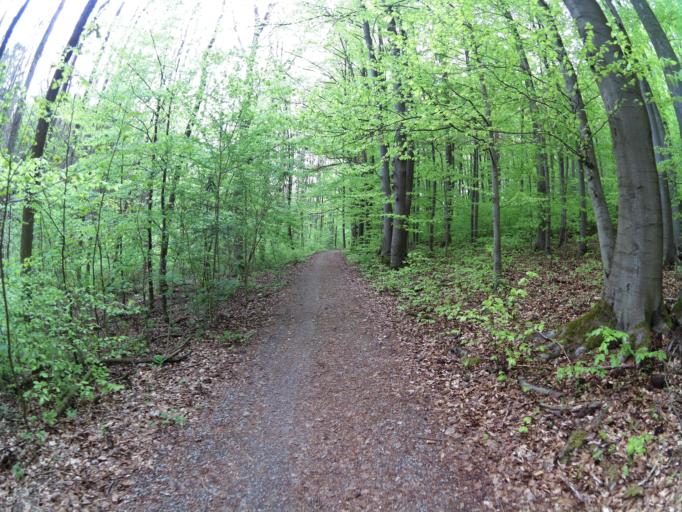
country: DE
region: Thuringia
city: Weberstedt
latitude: 51.0803
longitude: 10.5242
